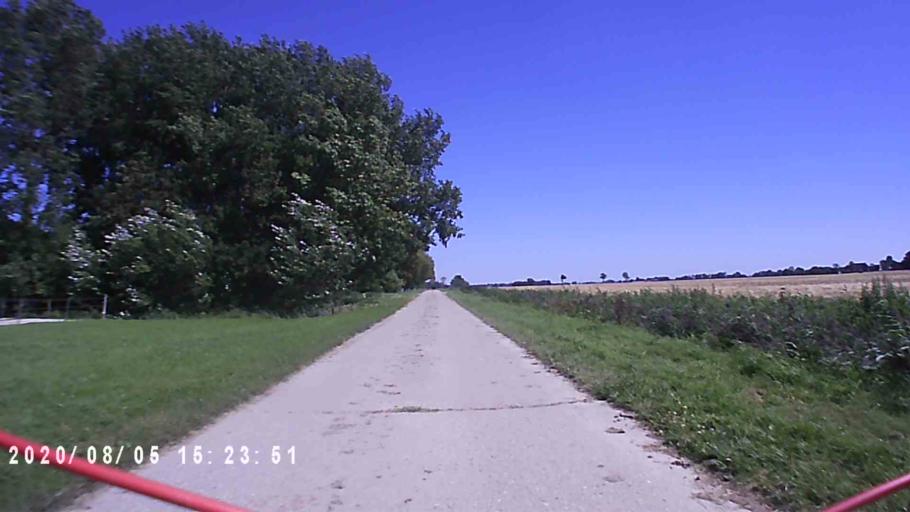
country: NL
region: Groningen
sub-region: Gemeente Zuidhorn
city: Oldehove
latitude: 53.3439
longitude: 6.4499
